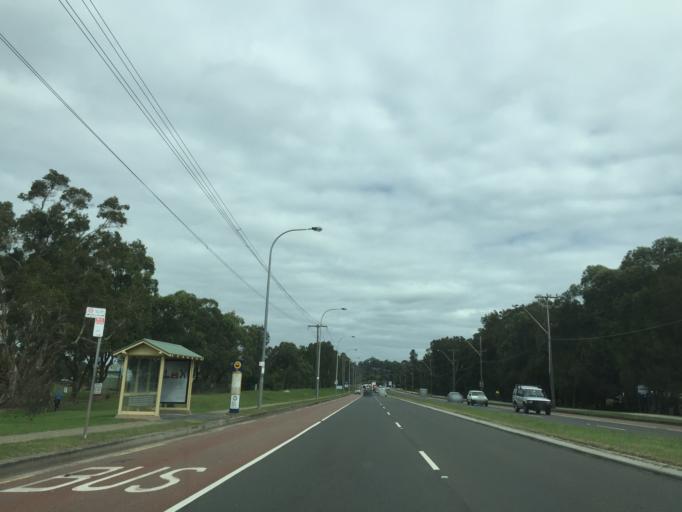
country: AU
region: New South Wales
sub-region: Pittwater
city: Warriewood
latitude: -33.6936
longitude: 151.3039
